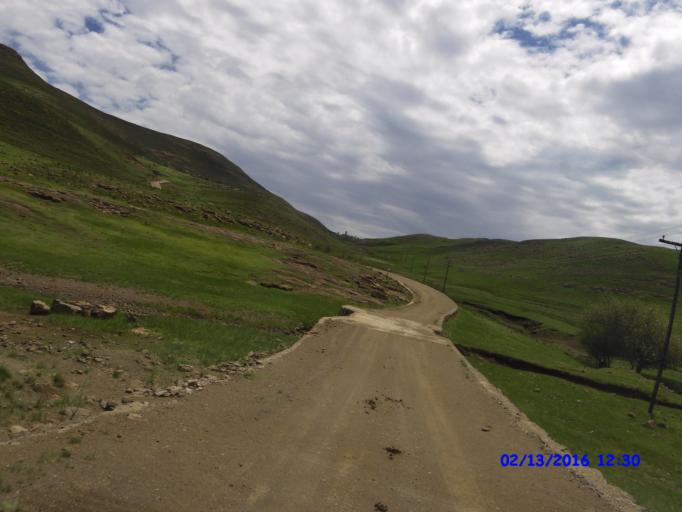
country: LS
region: Maseru
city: Nako
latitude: -29.8582
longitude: 28.0366
